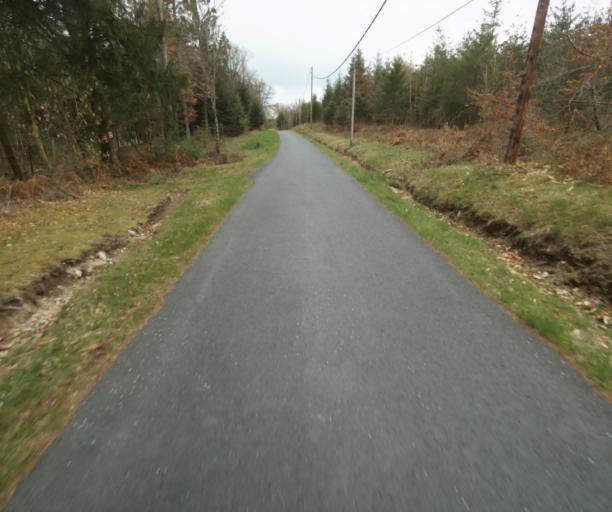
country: FR
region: Limousin
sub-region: Departement de la Correze
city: Correze
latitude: 45.3023
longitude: 1.9123
